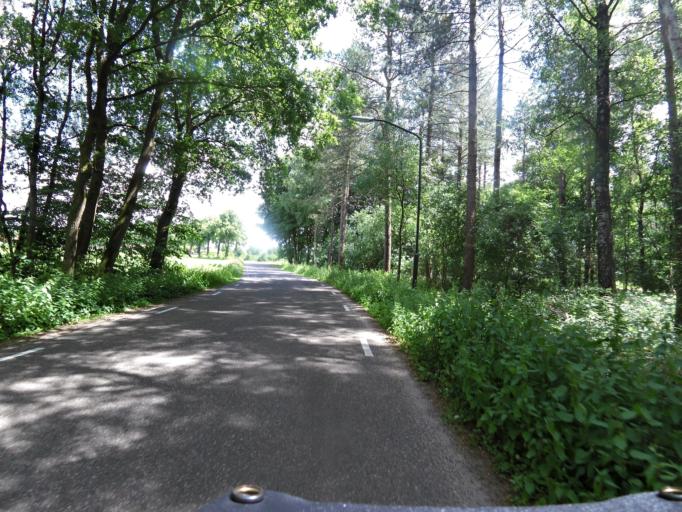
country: BE
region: Flanders
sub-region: Provincie Antwerpen
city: Arendonk
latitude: 51.3811
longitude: 5.1152
